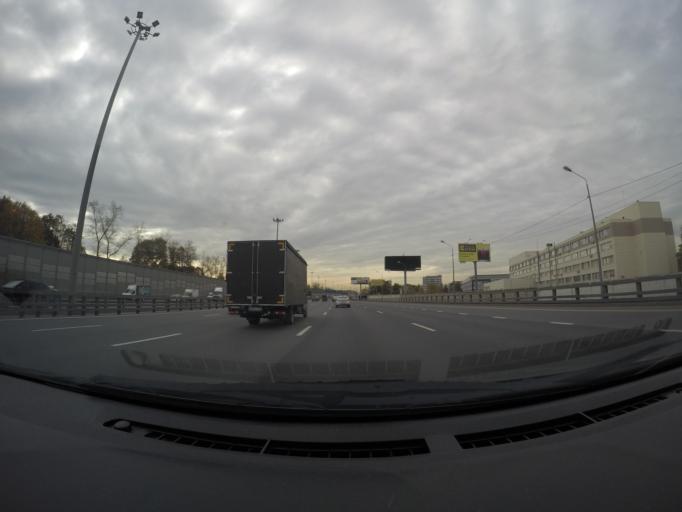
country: RU
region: Moskovskaya
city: Druzhba
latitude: 55.9051
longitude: 37.7616
